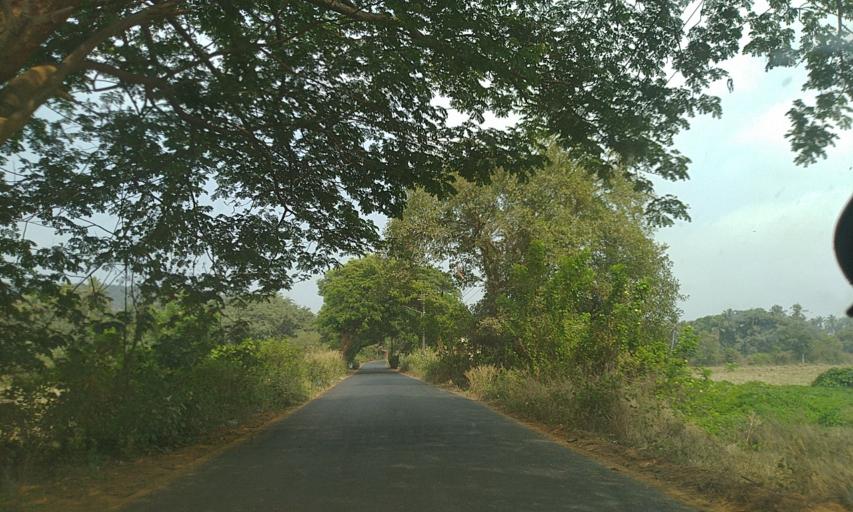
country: IN
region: Goa
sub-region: South Goa
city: Raia
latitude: 15.3079
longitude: 73.9604
